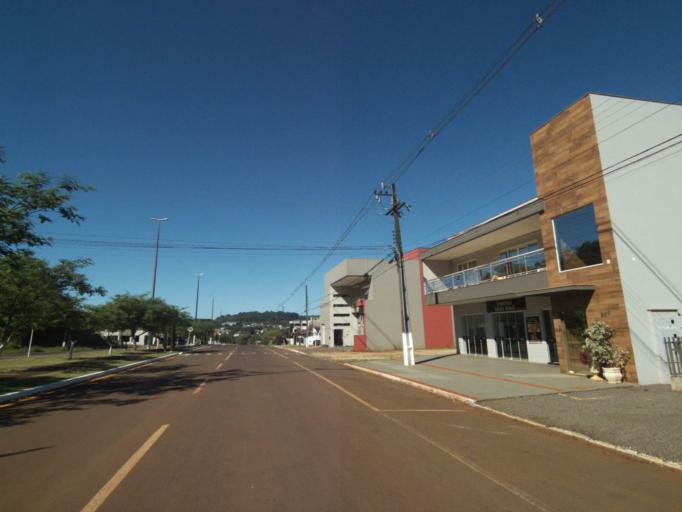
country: BR
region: Parana
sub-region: Pato Branco
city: Pato Branco
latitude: -26.2602
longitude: -52.7753
